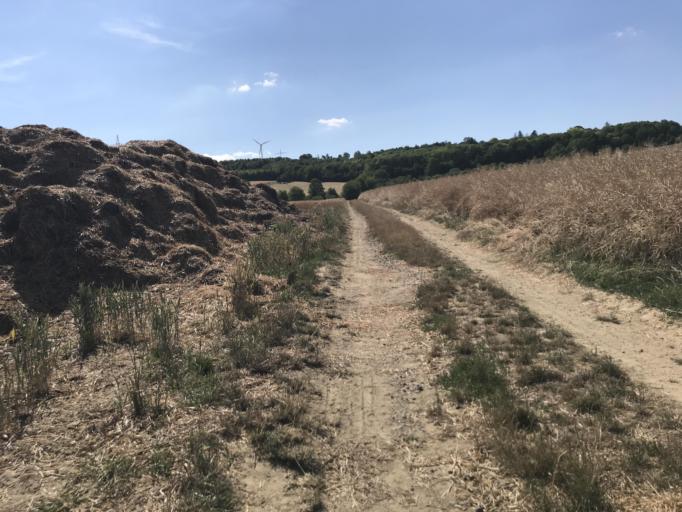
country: DE
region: Rheinland-Pfalz
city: Nieder-Olm
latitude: 49.9225
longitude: 8.2148
